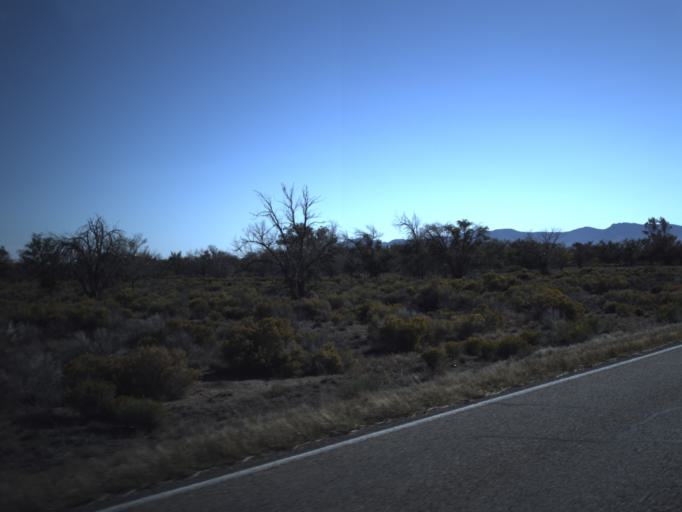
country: US
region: Utah
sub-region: Washington County
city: Enterprise
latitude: 37.7181
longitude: -113.6802
